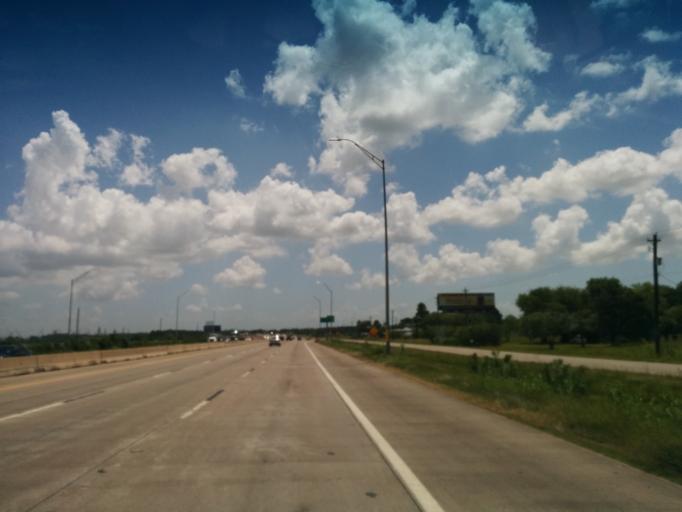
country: US
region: Texas
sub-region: Chambers County
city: Mont Belvieu
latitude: 29.8105
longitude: -94.9476
